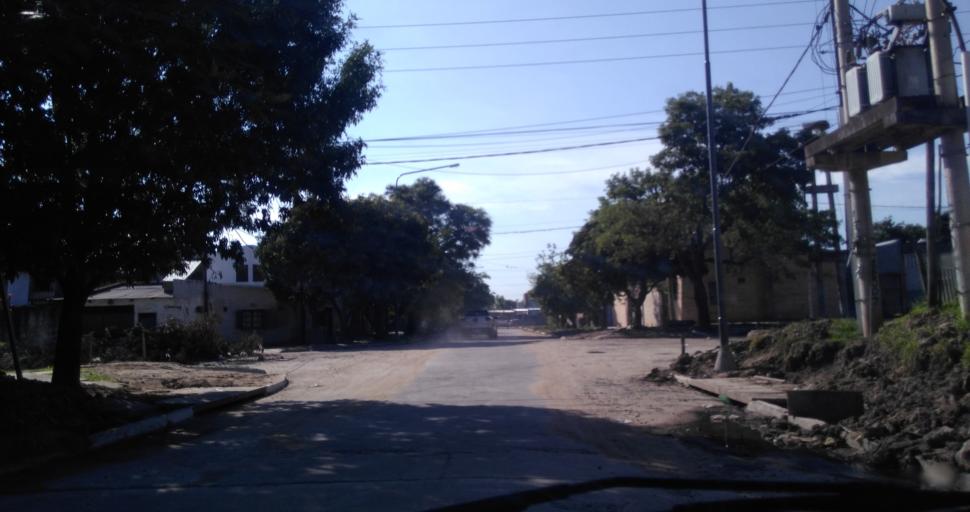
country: AR
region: Chaco
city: Resistencia
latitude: -27.4654
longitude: -58.9669
